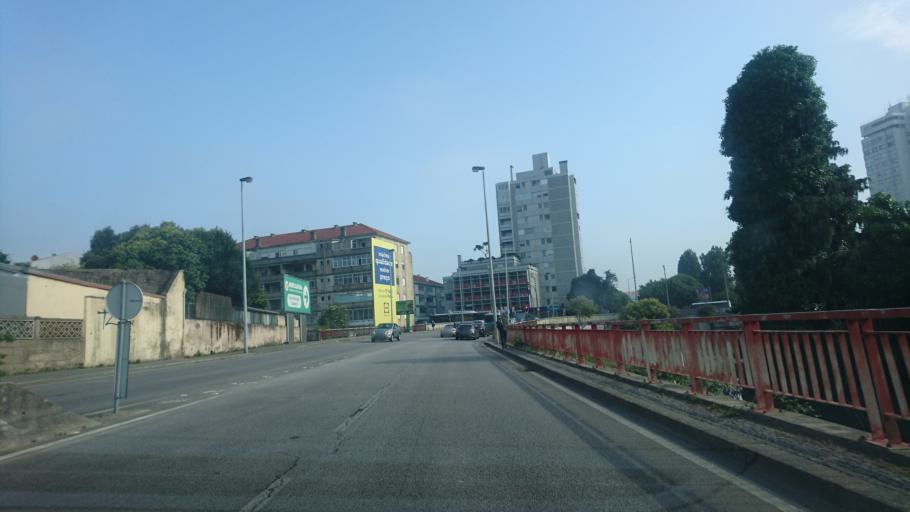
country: PT
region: Porto
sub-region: Matosinhos
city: Senhora da Hora
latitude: 41.1604
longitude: -8.6502
